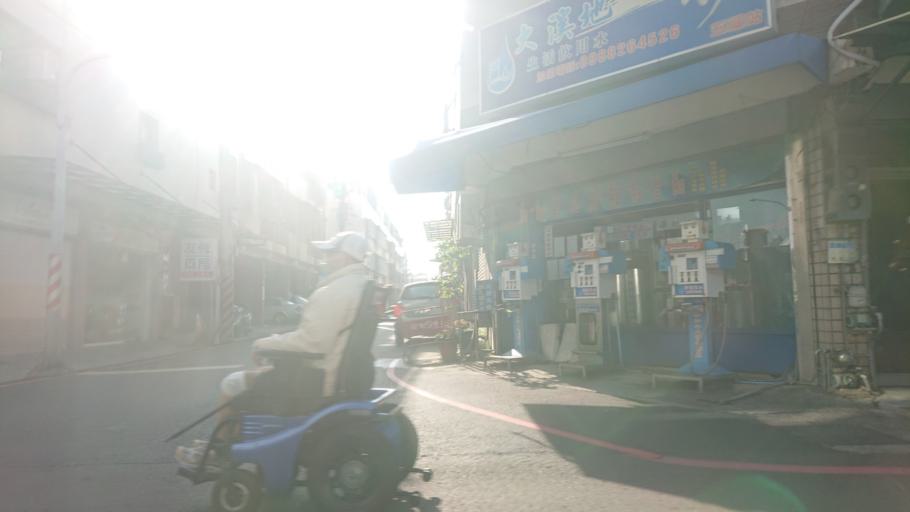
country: TW
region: Taiwan
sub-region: Tainan
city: Tainan
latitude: 23.0136
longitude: 120.2345
